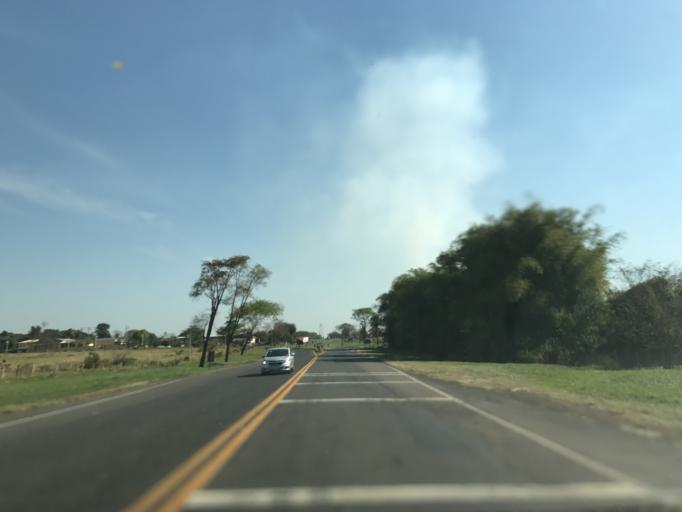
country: BR
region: Sao Paulo
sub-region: Penapolis
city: Penapolis
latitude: -21.3830
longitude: -50.0924
